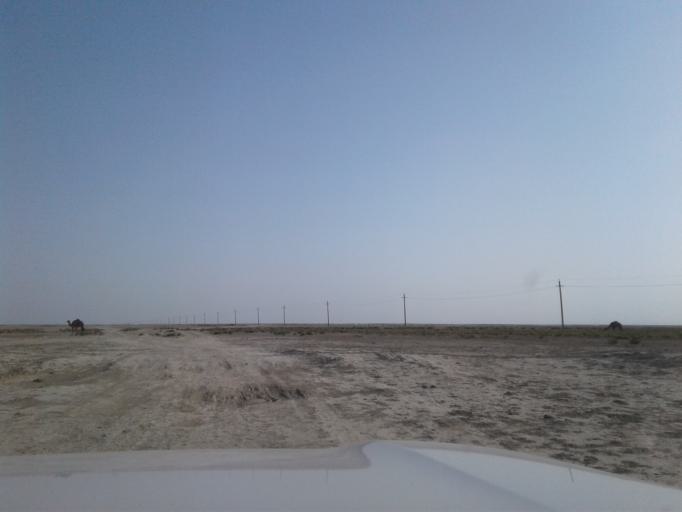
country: IR
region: Golestan
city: Aq Qayeh
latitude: 37.9960
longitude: 54.7408
